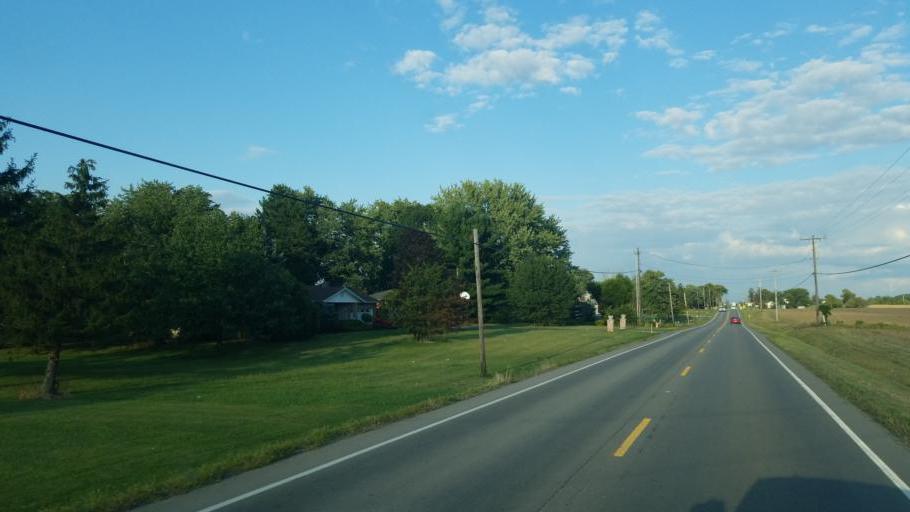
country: US
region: Ohio
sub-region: Huron County
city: Willard
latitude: 41.0527
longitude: -82.6915
